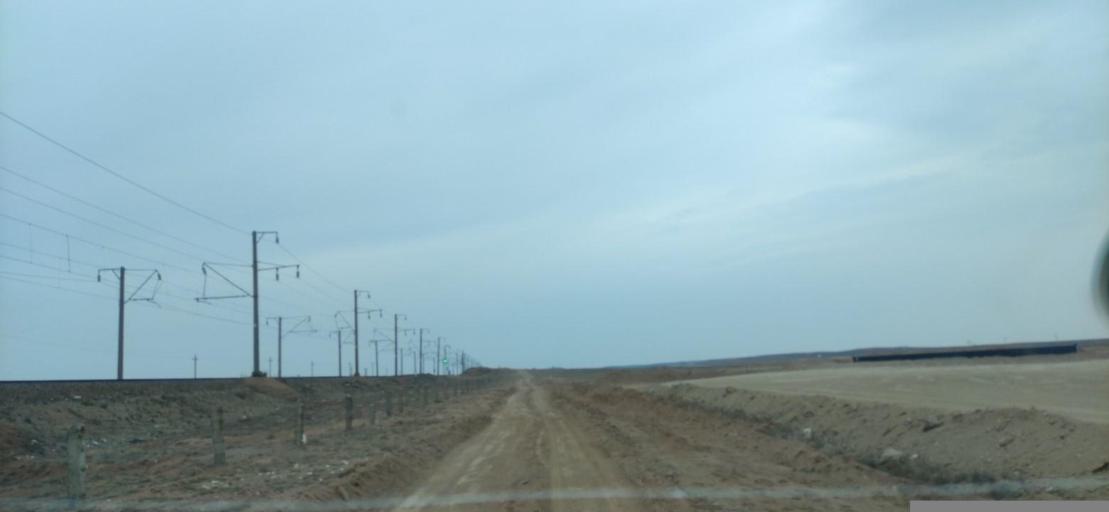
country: KZ
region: Qaraghandy
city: Saryshaghan
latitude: 46.1392
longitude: 73.6057
